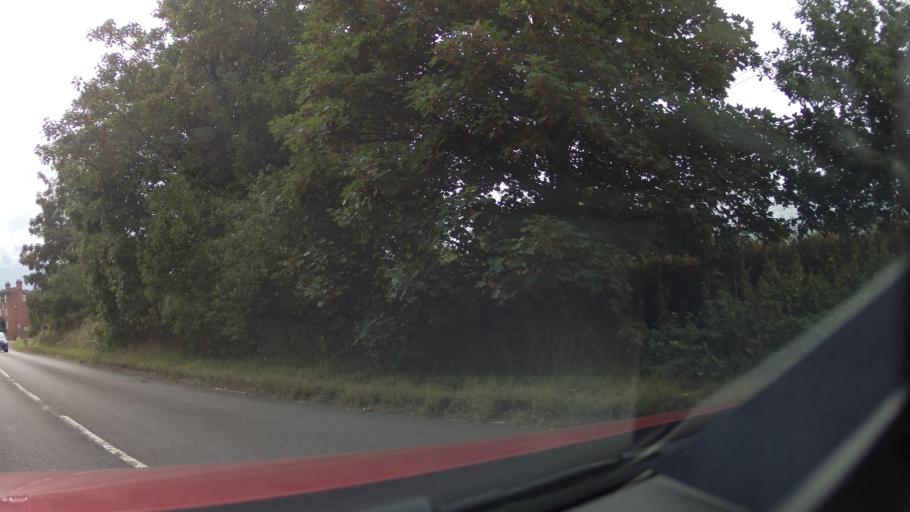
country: GB
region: England
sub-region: Telford and Wrekin
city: Newport
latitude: 52.7889
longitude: -2.3650
